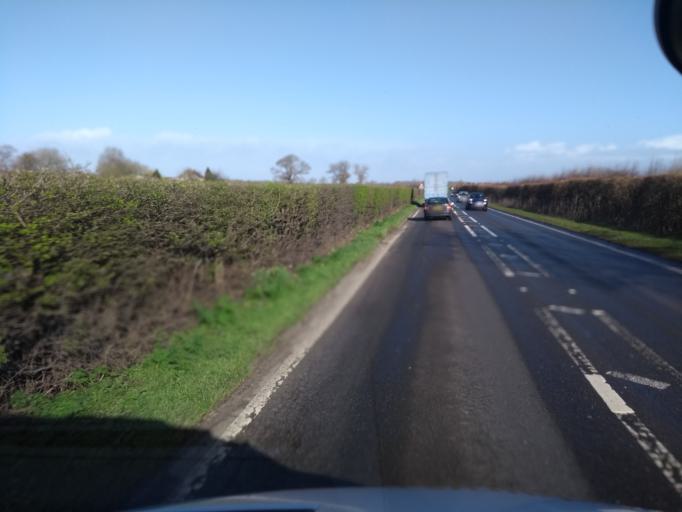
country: GB
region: England
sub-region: Somerset
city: Ilchester
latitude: 50.9899
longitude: -2.6778
